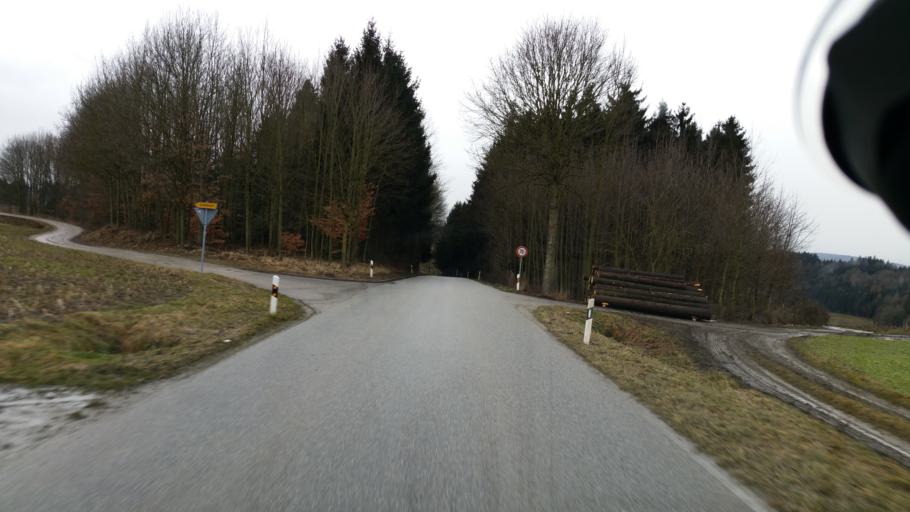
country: DE
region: Bavaria
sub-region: Lower Bavaria
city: Eching
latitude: 48.4907
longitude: 12.0799
